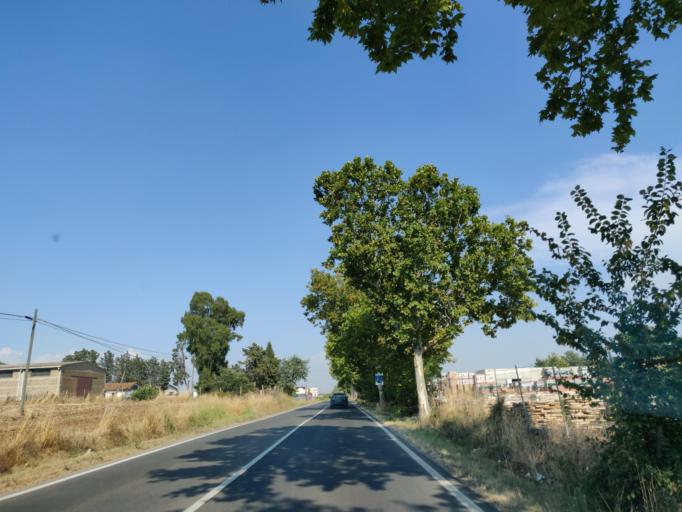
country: IT
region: Latium
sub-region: Provincia di Viterbo
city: Montalto di Castro
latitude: 42.3502
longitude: 11.6214
